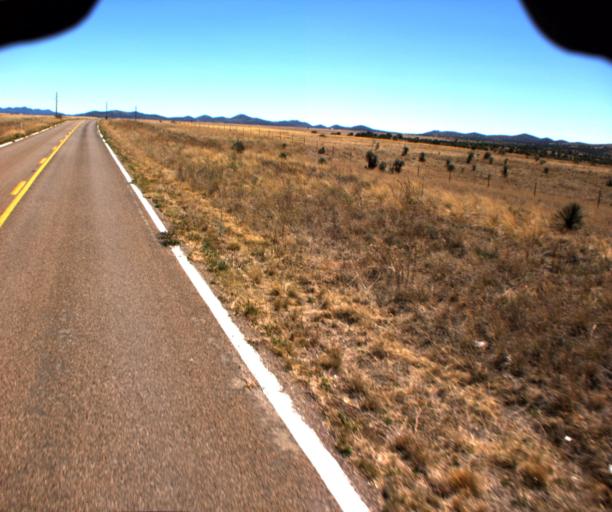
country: US
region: Arizona
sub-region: Cochise County
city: Huachuca City
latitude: 31.6485
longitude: -110.6025
